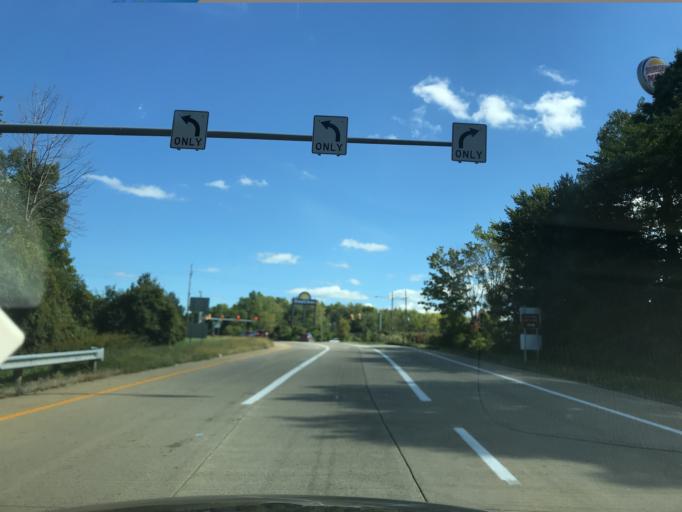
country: US
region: Ohio
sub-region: Lake County
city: Kirtland
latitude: 41.6393
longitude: -81.3747
